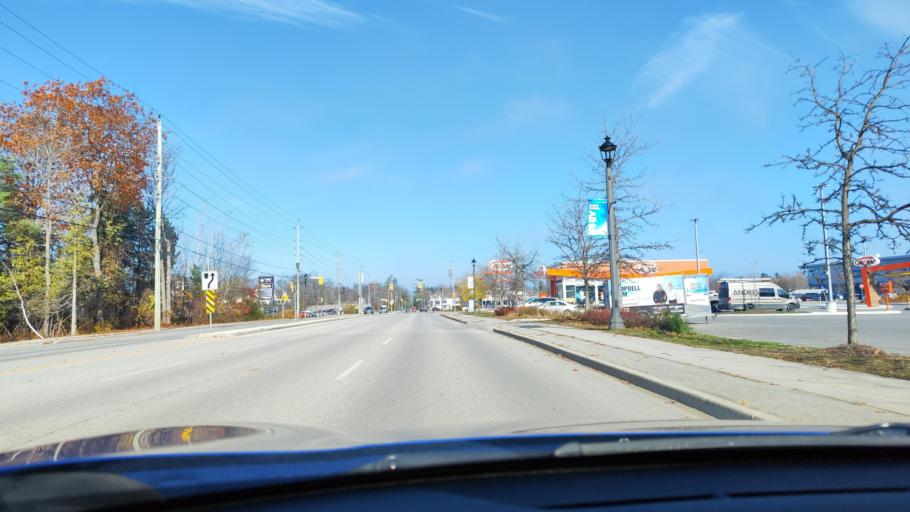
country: CA
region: Ontario
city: Wasaga Beach
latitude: 44.4713
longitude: -80.0755
